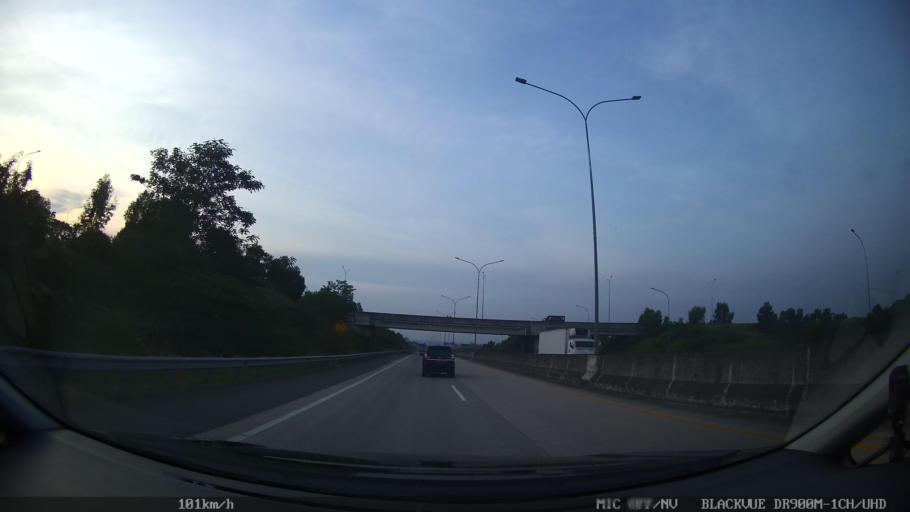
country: ID
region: Lampung
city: Penengahan
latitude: -5.8069
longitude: 105.7332
